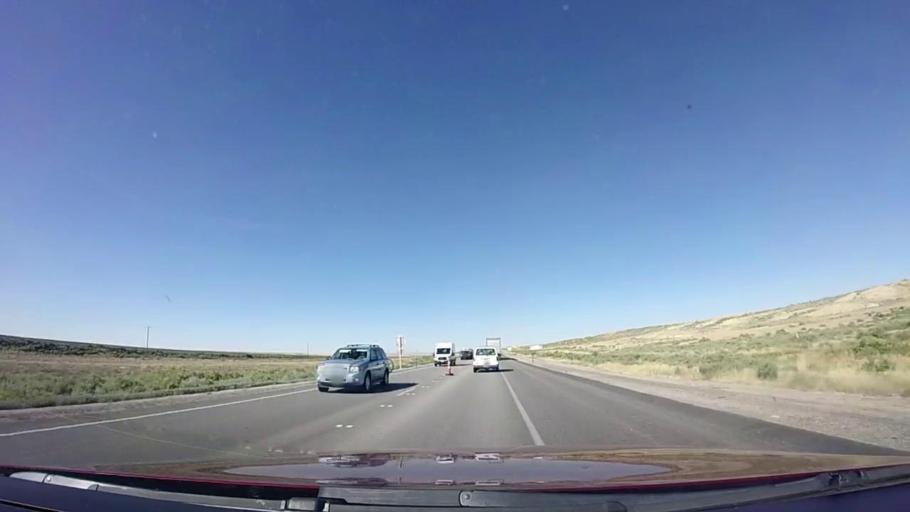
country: US
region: Wyoming
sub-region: Carbon County
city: Rawlins
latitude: 41.7014
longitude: -107.9082
